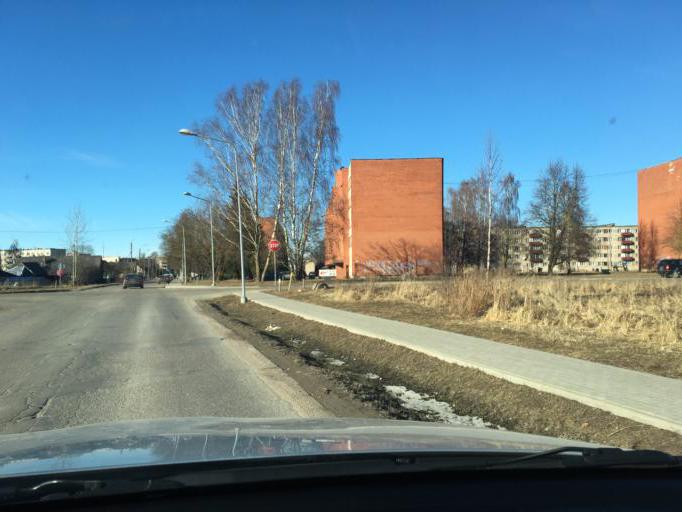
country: LV
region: Jekabpils Rajons
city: Jekabpils
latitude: 56.4878
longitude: 25.8660
